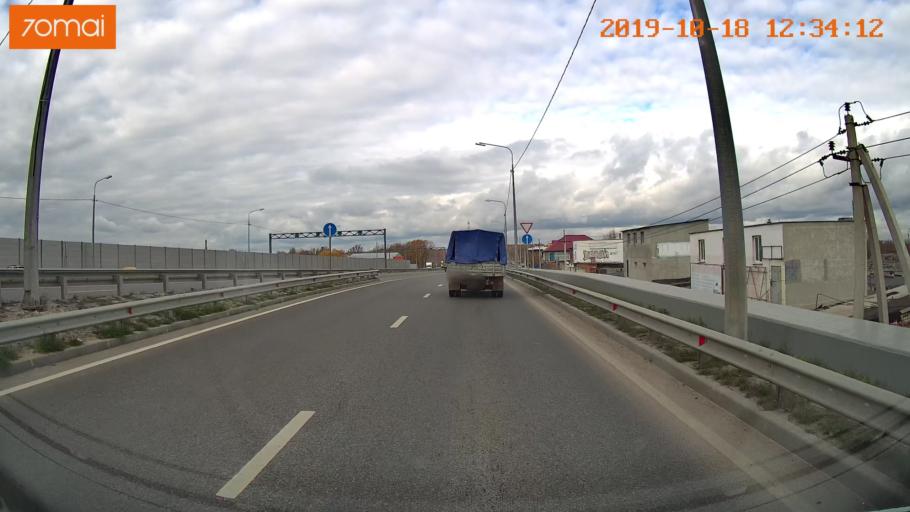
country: RU
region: Rjazan
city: Ryazan'
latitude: 54.6118
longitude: 39.6390
